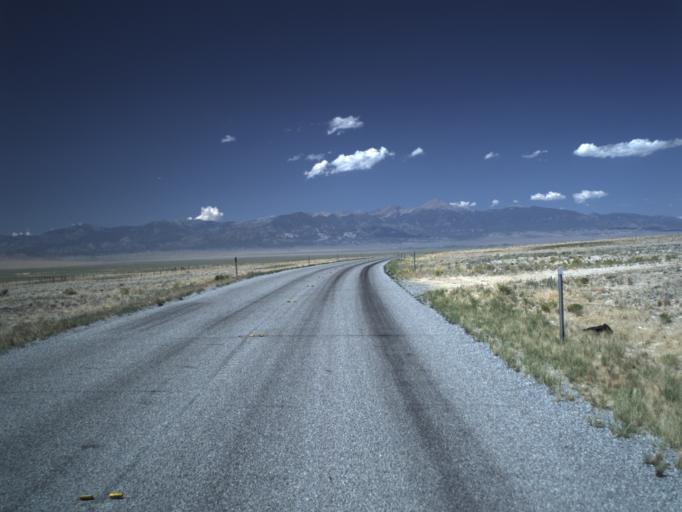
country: US
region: Utah
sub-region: Beaver County
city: Milford
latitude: 39.0400
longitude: -113.8146
